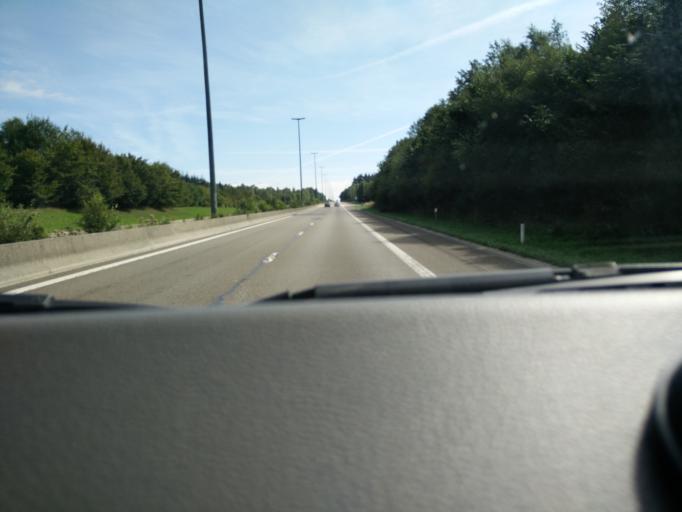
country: BE
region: Wallonia
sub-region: Province du Luxembourg
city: Neufchateau
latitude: 49.8851
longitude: 5.4004
